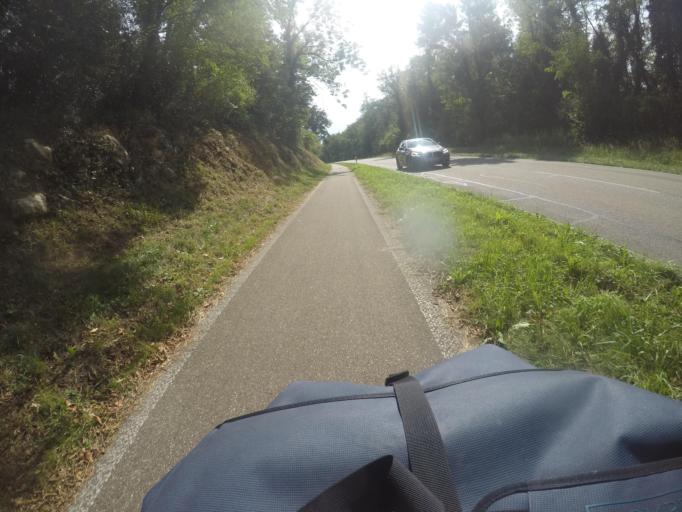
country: FR
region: Alsace
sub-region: Departement du Haut-Rhin
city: Kembs
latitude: 47.6704
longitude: 7.5292
